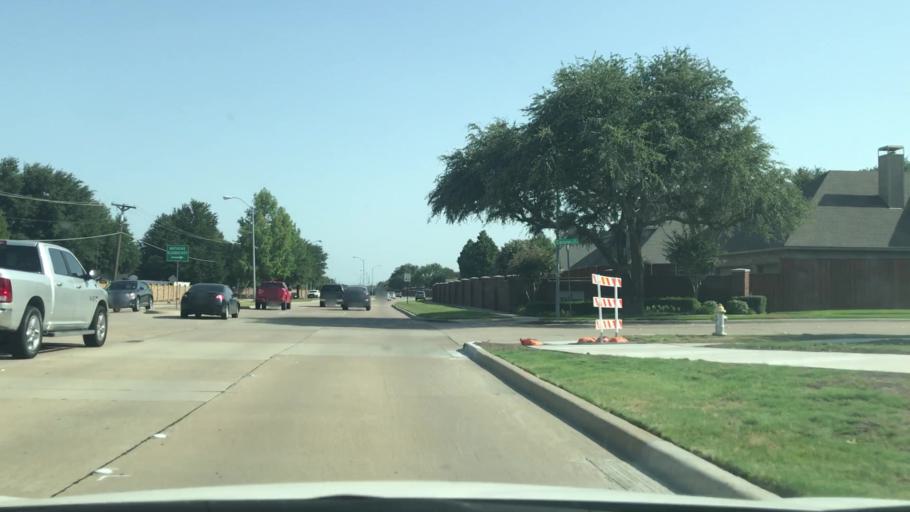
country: US
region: Texas
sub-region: Collin County
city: Plano
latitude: 33.0794
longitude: -96.7502
